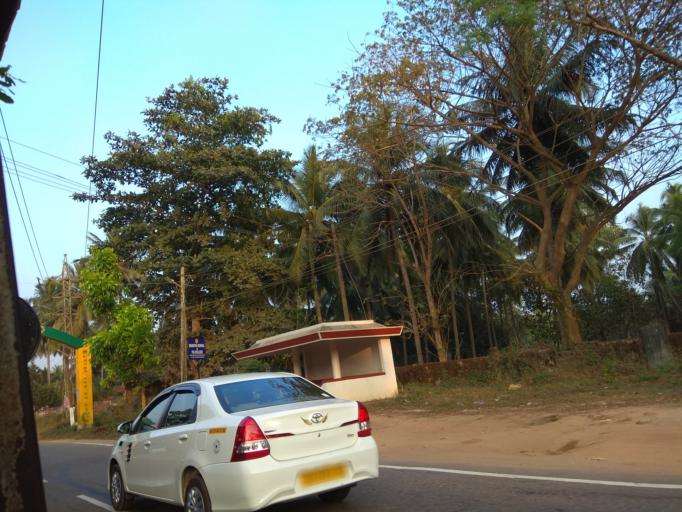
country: IN
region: Karnataka
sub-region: Dakshina Kannada
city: Mangalore
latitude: 12.9381
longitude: 74.8636
